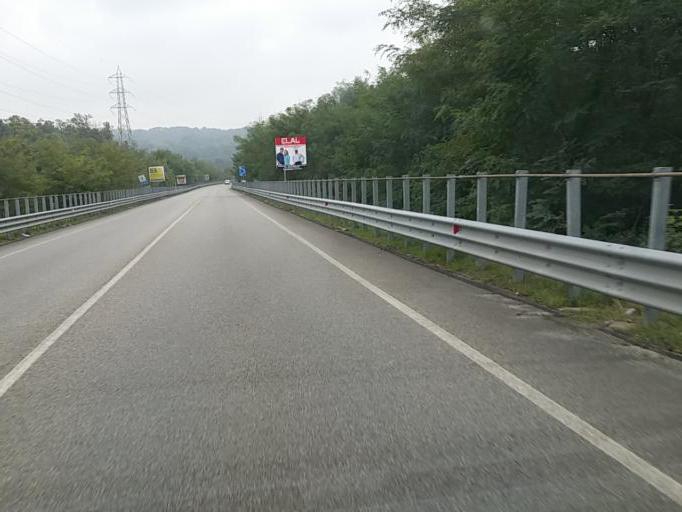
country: IT
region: Piedmont
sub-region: Provincia di Novara
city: Briga Novarese
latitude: 45.7236
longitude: 8.4561
